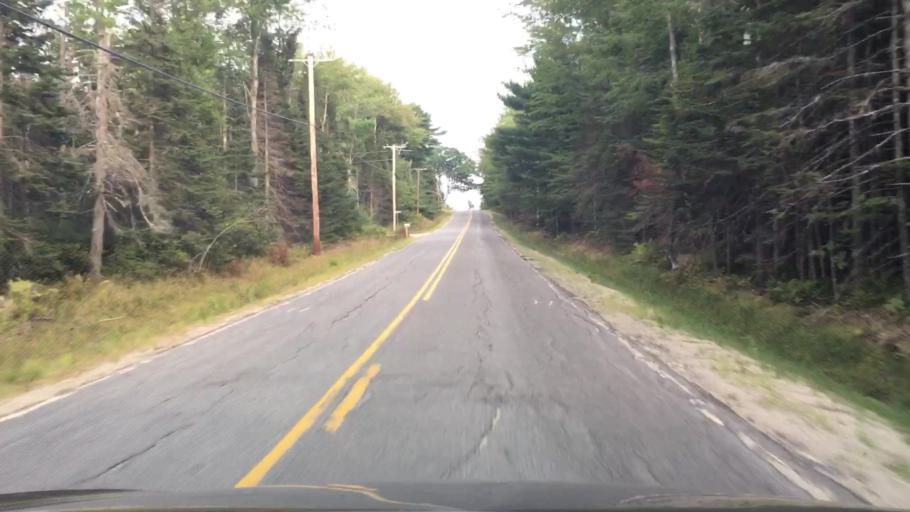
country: US
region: Maine
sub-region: Hancock County
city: Surry
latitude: 44.5004
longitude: -68.5696
